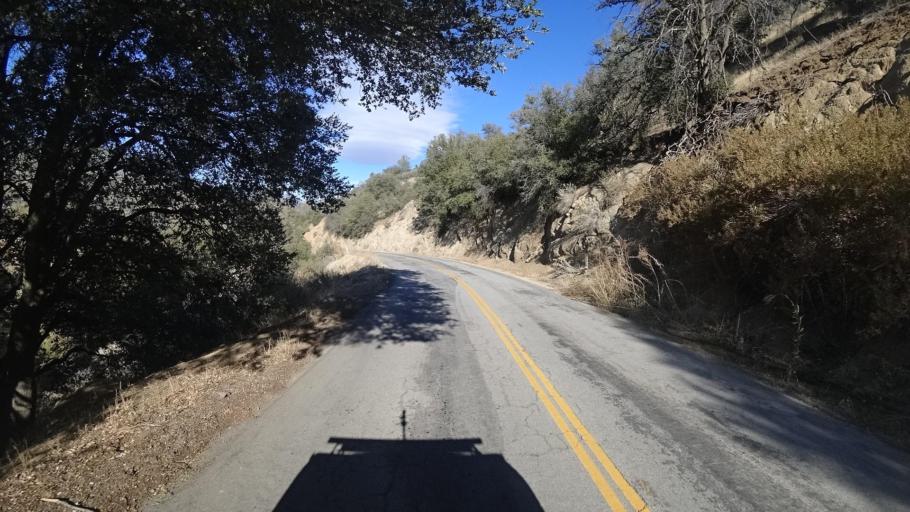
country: US
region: California
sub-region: Kern County
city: Bodfish
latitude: 35.4724
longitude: -118.5311
